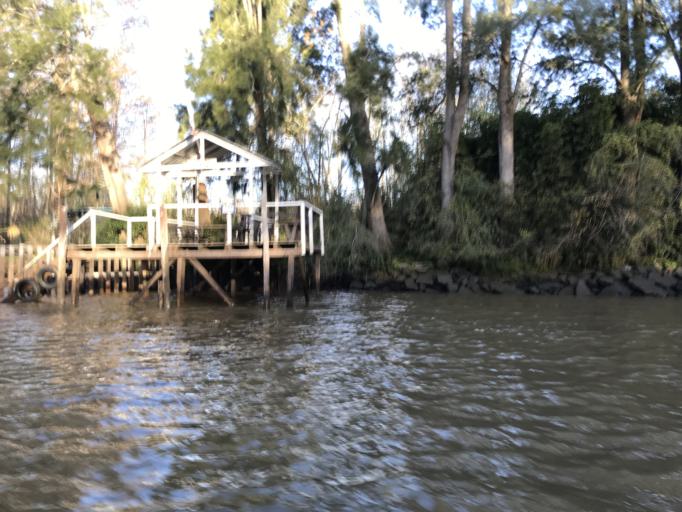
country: AR
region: Buenos Aires
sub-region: Partido de Tigre
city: Tigre
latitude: -34.3730
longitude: -58.5849
